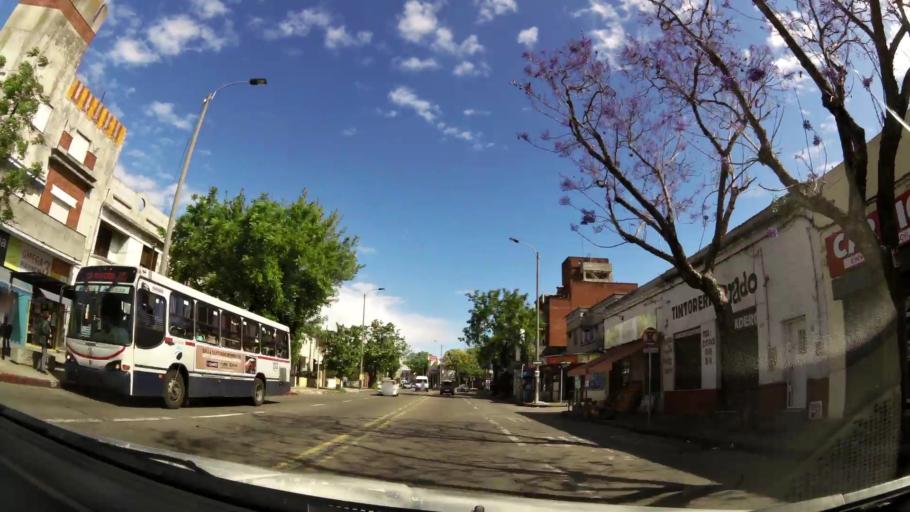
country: UY
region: Montevideo
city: Montevideo
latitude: -34.8687
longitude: -56.1918
